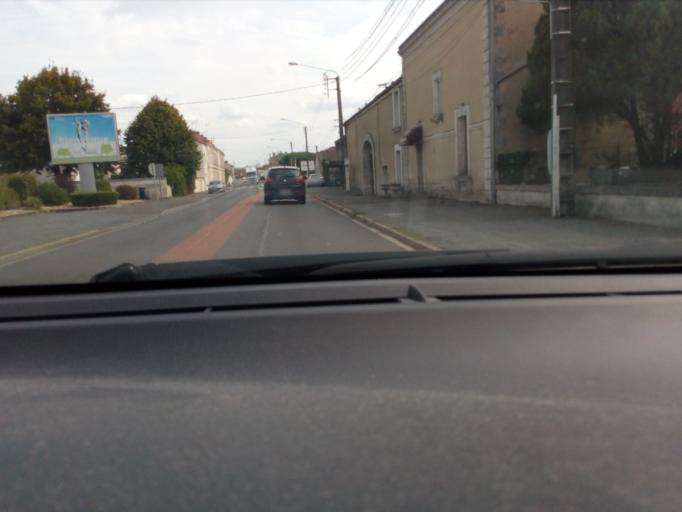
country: FR
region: Poitou-Charentes
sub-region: Departement de la Charente
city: Saint-Yrieix-sur-Charente
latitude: 45.6681
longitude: 0.1200
